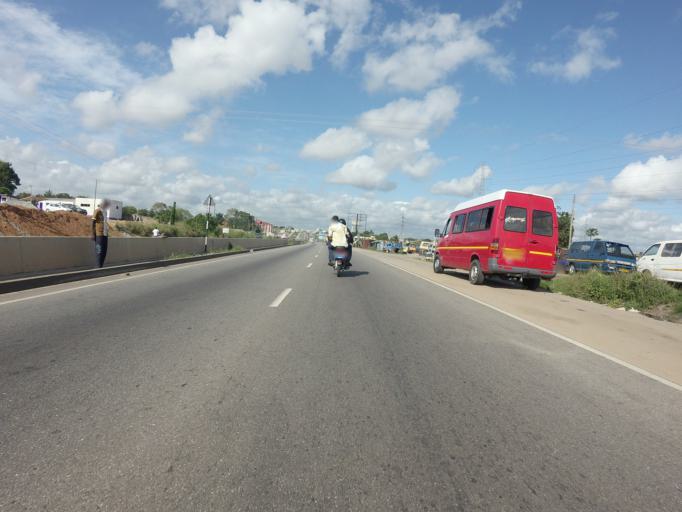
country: GH
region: Central
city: Kasoa
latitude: 5.5321
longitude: -0.4412
